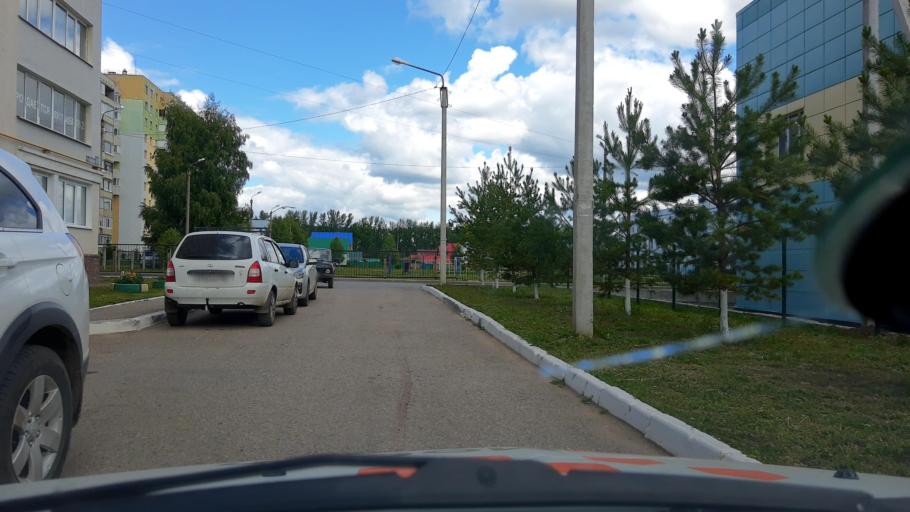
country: RU
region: Bashkortostan
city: Blagoveshchensk
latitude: 55.0492
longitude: 55.9634
